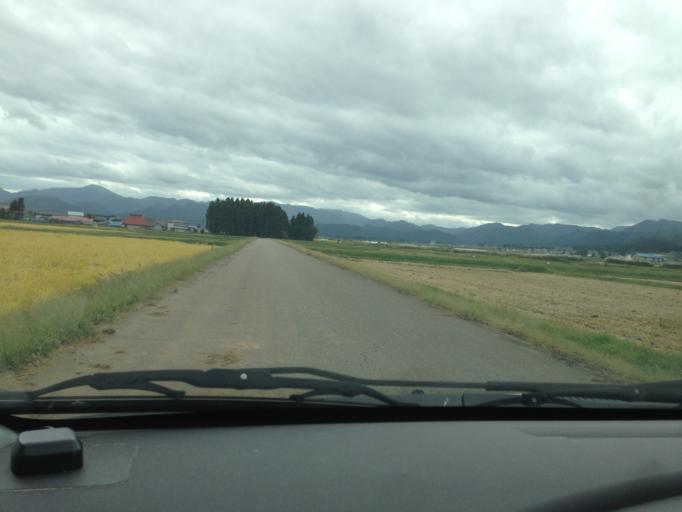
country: JP
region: Fukushima
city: Kitakata
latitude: 37.4977
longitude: 139.8299
